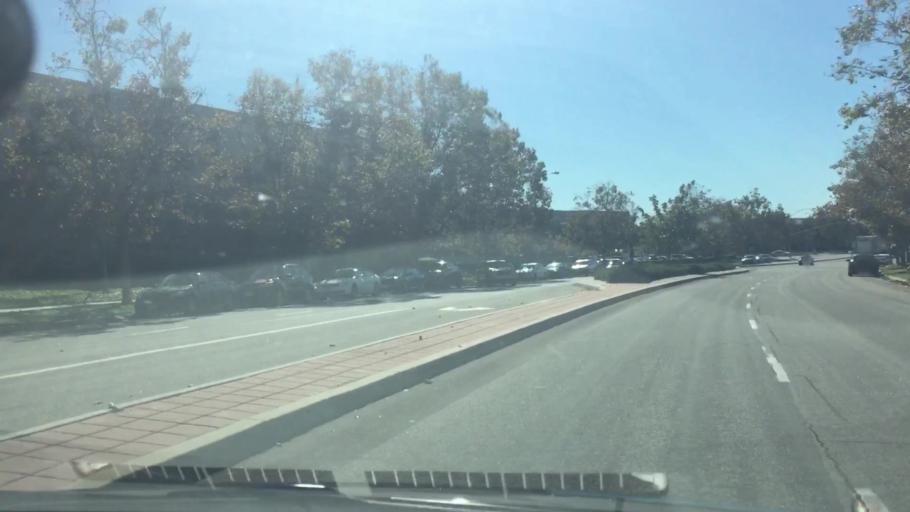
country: US
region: California
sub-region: Orange County
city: Rancho Santa Margarita
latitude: 33.6329
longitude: -117.6046
